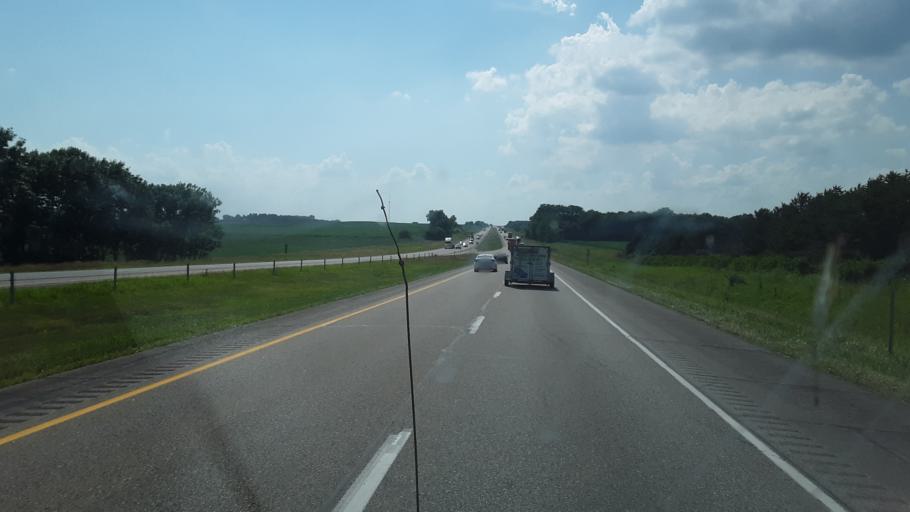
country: US
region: Iowa
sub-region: Cedar County
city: West Branch
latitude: 41.6637
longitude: -91.2805
